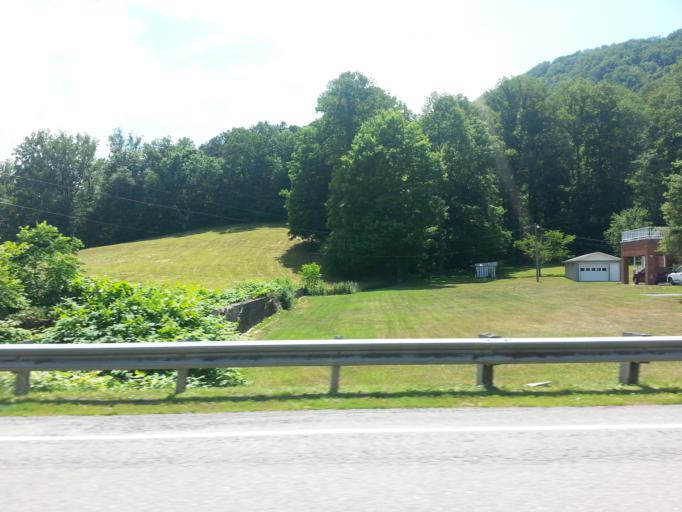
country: US
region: Virginia
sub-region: Lee County
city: Pennington Gap
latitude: 36.7724
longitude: -83.0326
